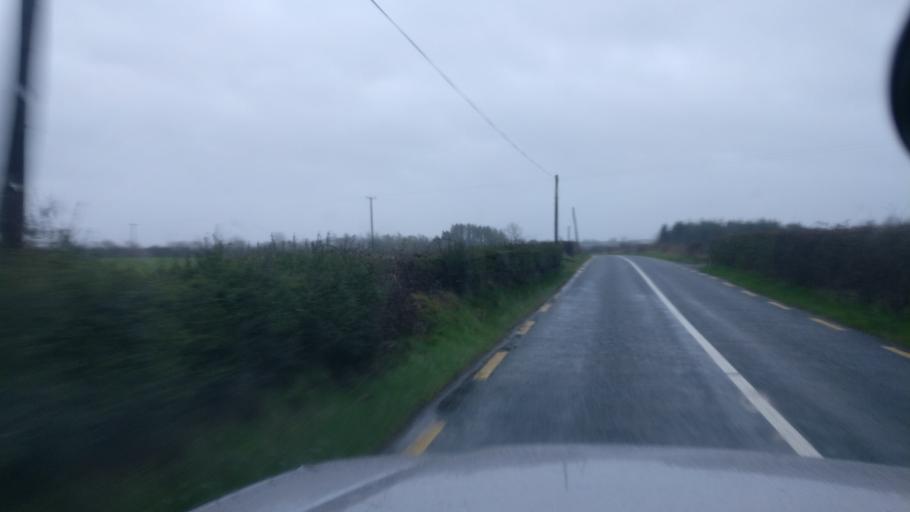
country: IE
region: Connaught
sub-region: County Galway
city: Portumna
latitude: 53.2033
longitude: -8.1963
